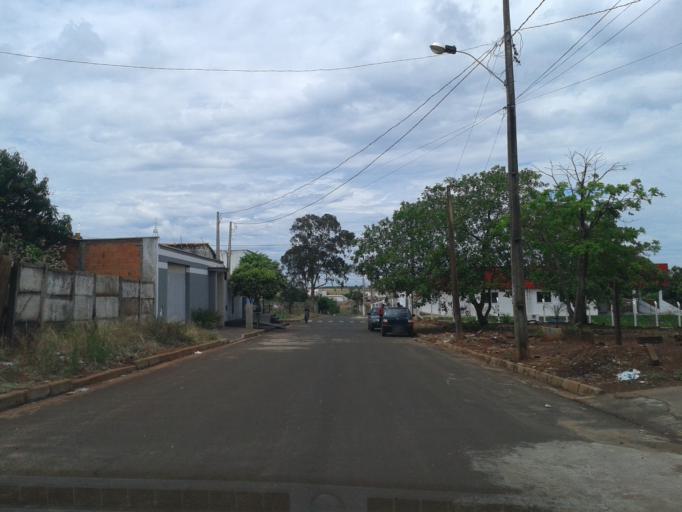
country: BR
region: Minas Gerais
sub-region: Ituiutaba
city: Ituiutaba
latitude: -18.9941
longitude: -49.4626
